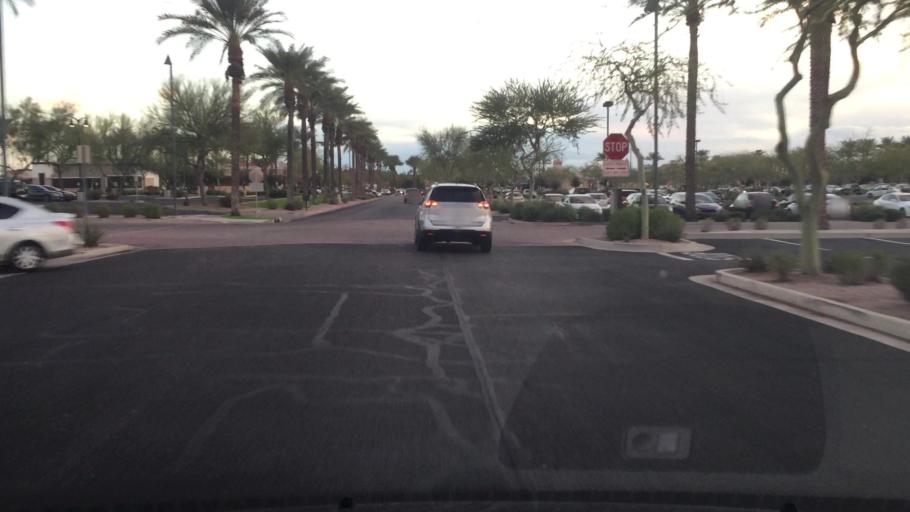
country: US
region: Arizona
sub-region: Maricopa County
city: Gilbert
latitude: 33.3828
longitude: -111.7552
